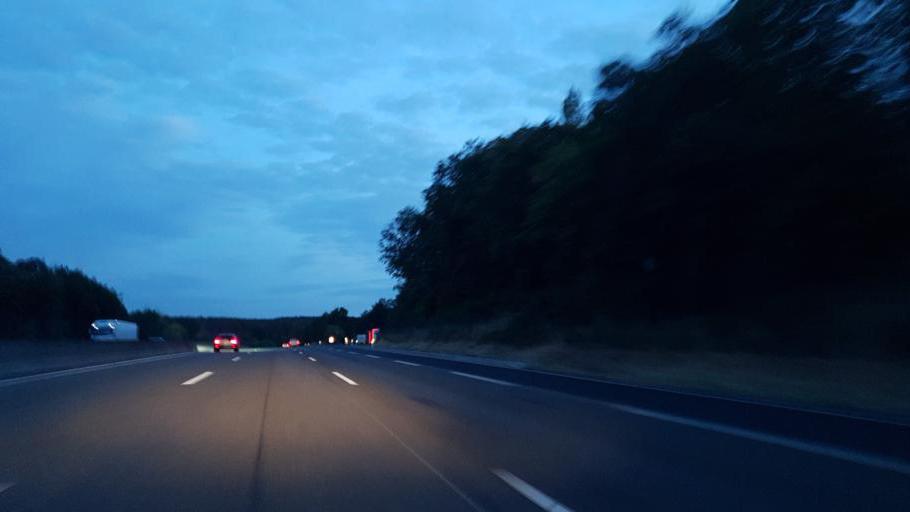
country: DE
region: Hesse
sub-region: Regierungsbezirk Kassel
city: Guxhagen
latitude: 51.1794
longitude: 9.4733
